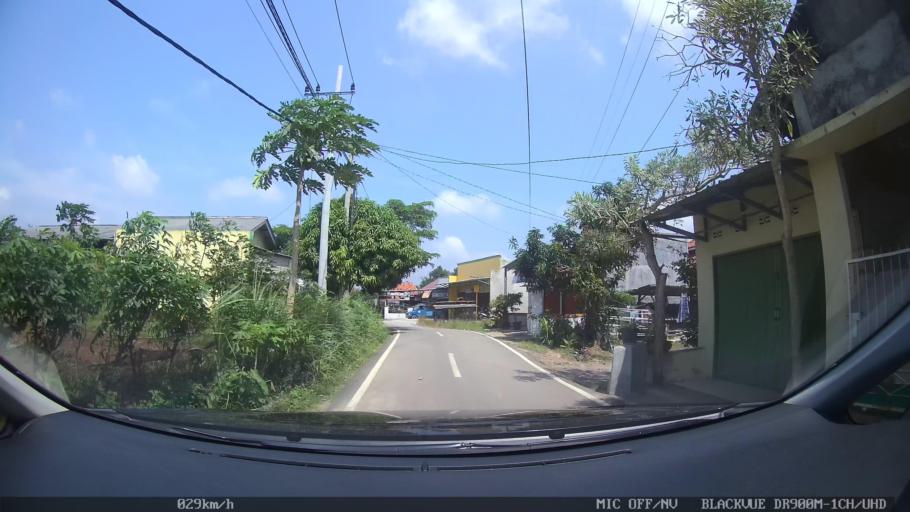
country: ID
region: Lampung
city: Kedaton
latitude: -5.3479
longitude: 105.2772
